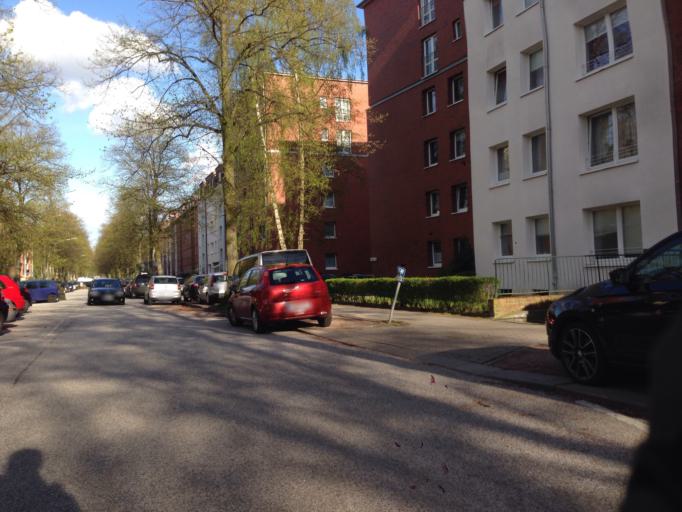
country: DE
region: Hamburg
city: Borgfelde
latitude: 53.5653
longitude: 10.0470
